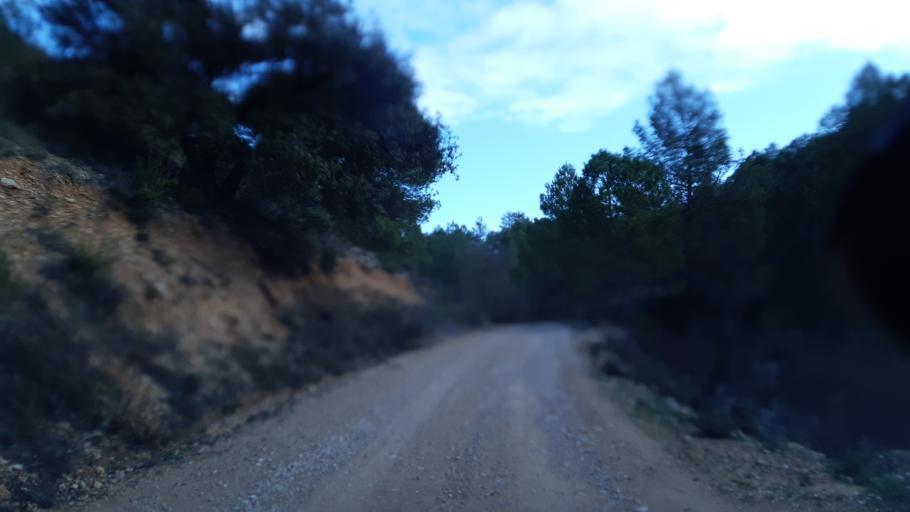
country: ES
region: Aragon
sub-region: Provincia de Teruel
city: Valderrobres
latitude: 40.8511
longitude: 0.2187
